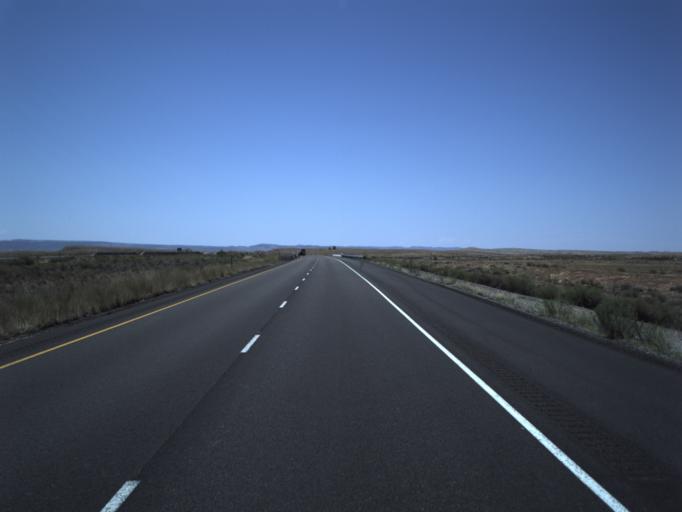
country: US
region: Colorado
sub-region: Mesa County
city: Loma
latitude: 39.0394
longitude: -109.2813
